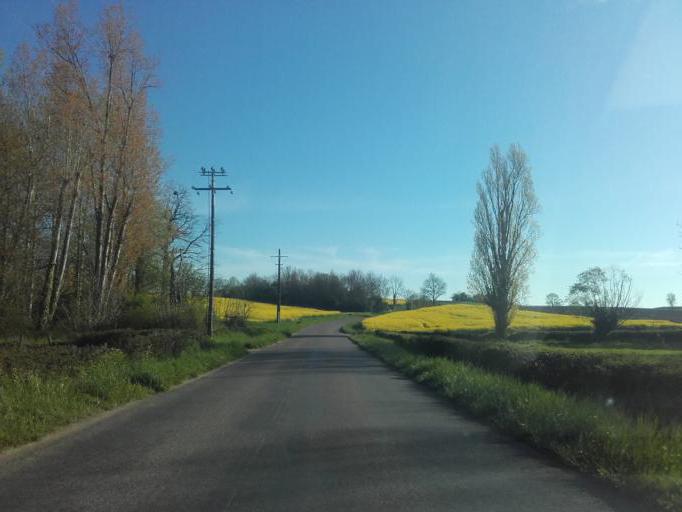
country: FR
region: Bourgogne
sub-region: Departement de Saone-et-Loire
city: Mellecey
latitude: 46.8142
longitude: 4.7354
